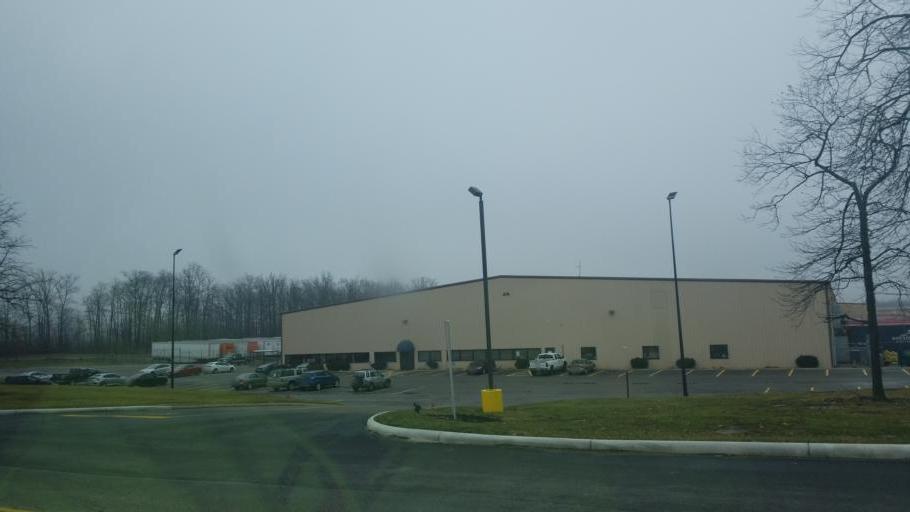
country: US
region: Ohio
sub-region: Champaign County
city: North Lewisburg
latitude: 40.2829
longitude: -83.5508
